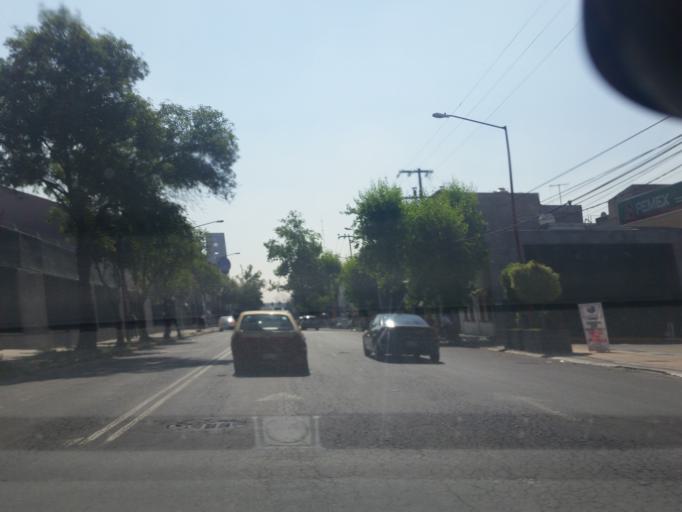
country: MX
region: Mexico City
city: Cuauhtemoc
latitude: 19.4554
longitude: -99.1611
